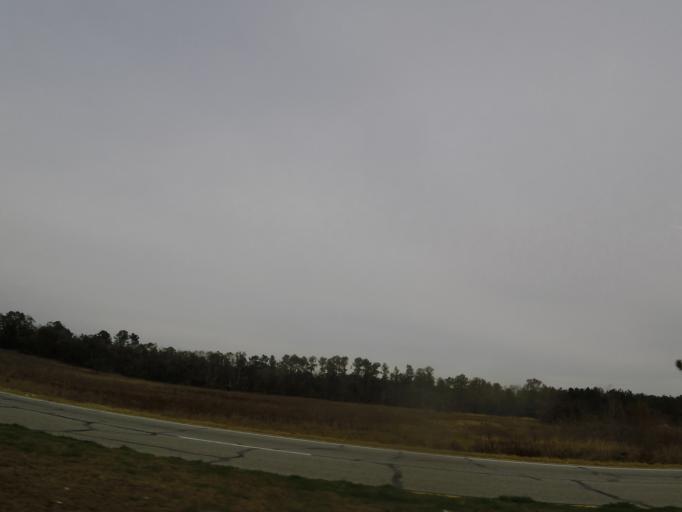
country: US
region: Georgia
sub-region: Decatur County
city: Bainbridge
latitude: 30.9234
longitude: -84.6111
